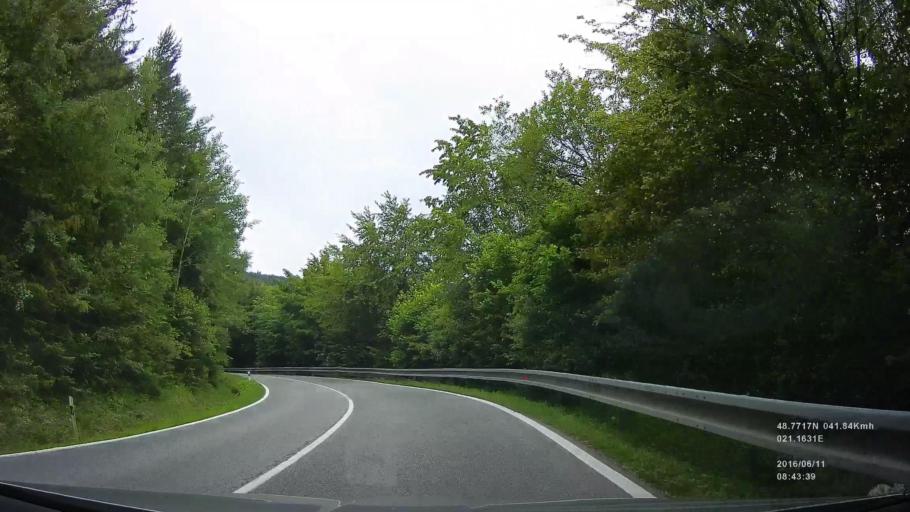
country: SK
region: Kosicky
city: Kosice
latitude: 48.7526
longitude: 21.2103
